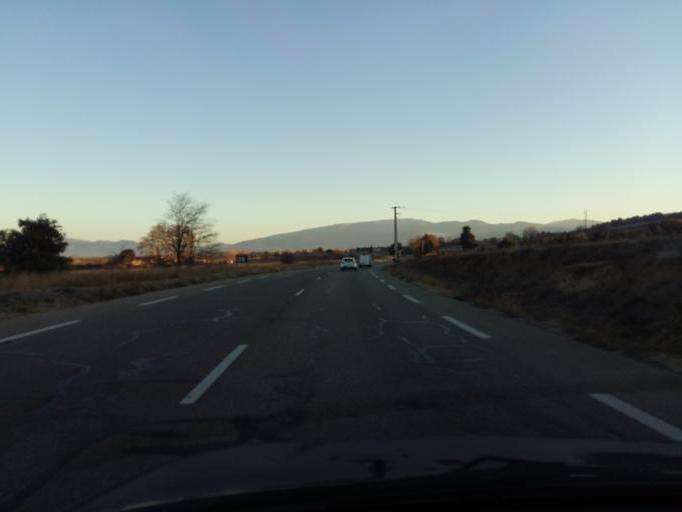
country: FR
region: Provence-Alpes-Cote d'Azur
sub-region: Departement du Vaucluse
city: Valreas
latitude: 44.3543
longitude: 4.9650
